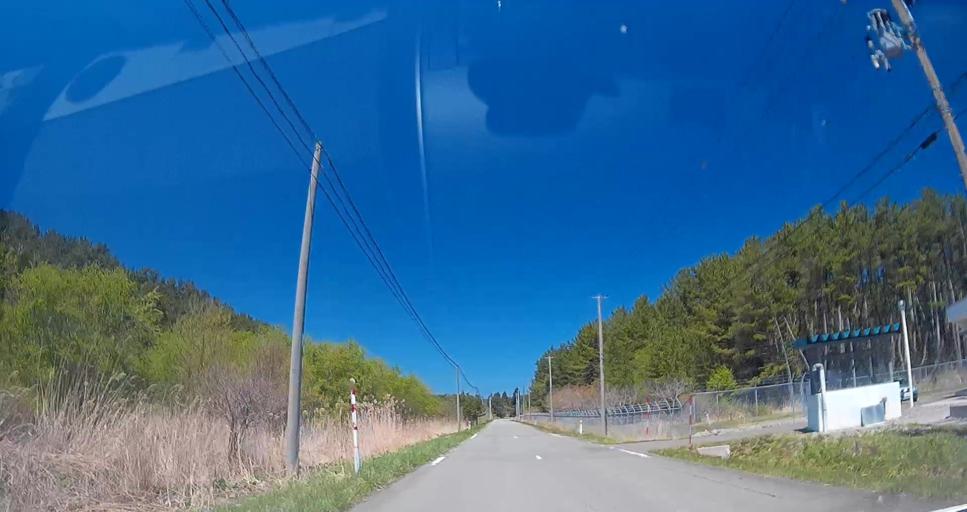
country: JP
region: Aomori
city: Mutsu
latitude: 41.2420
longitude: 141.3984
